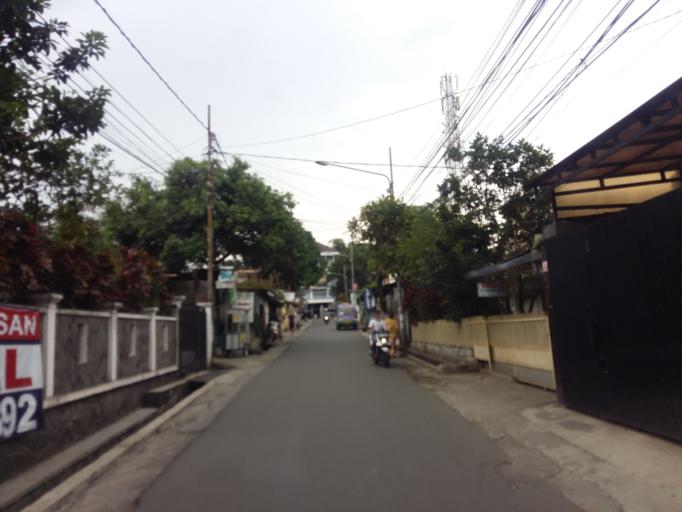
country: ID
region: West Java
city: Bandung
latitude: -6.8805
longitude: 107.6119
